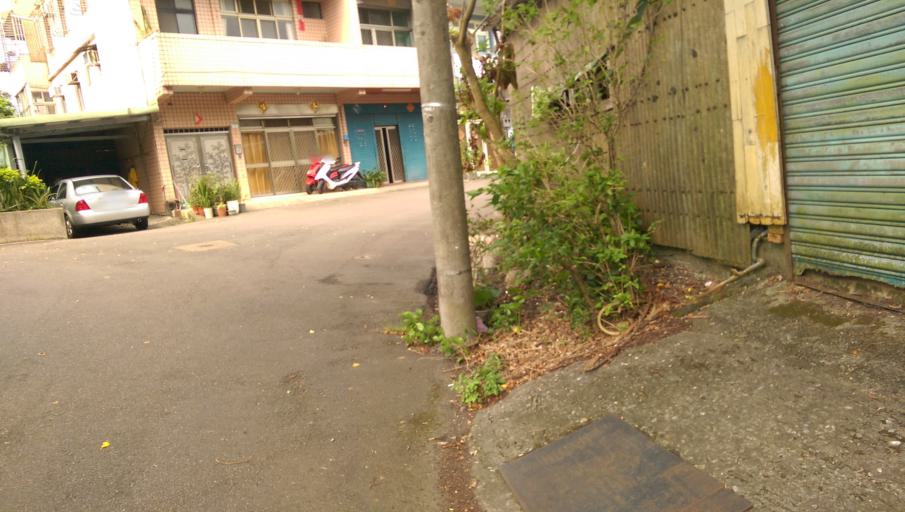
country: TW
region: Taipei
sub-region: Taipei
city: Banqiao
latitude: 24.9297
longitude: 121.5437
